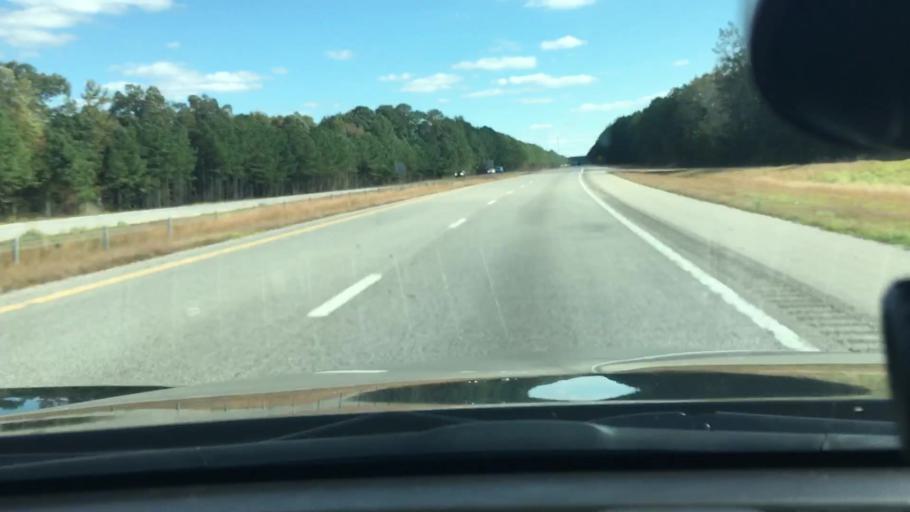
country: US
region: North Carolina
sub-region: Wilson County
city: Wilson
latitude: 35.6667
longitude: -77.7627
